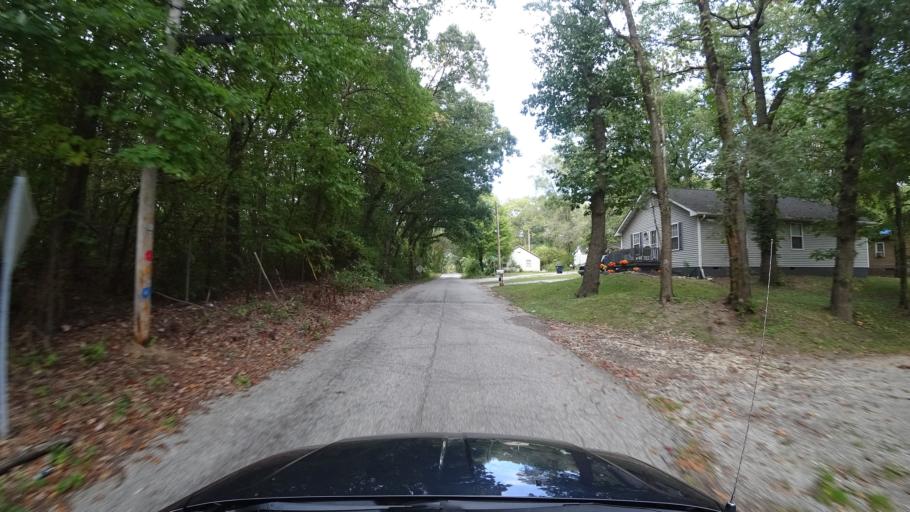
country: US
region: Indiana
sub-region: LaPorte County
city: Long Beach
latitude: 41.7288
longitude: -86.8579
